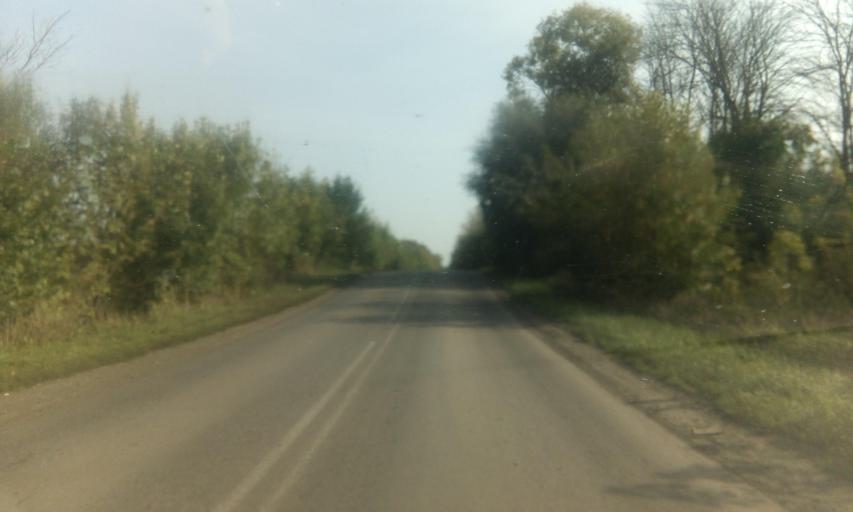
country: RU
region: Tula
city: Partizan
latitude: 53.9714
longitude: 38.1138
